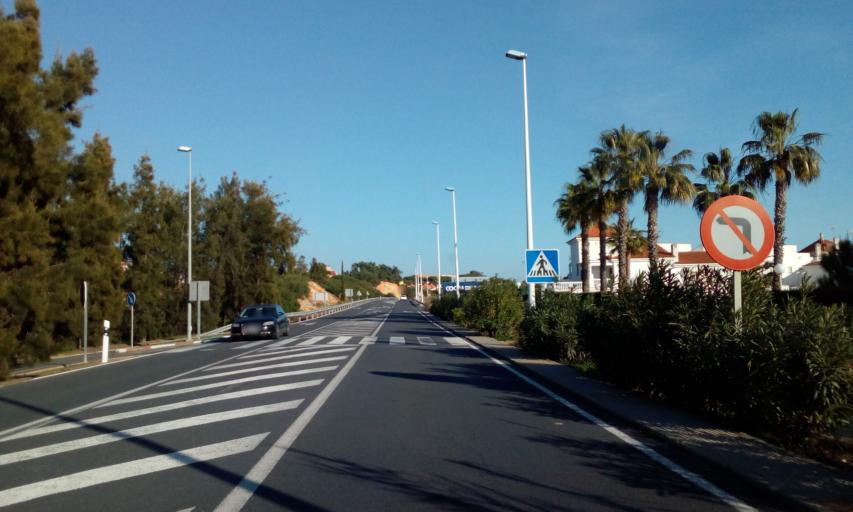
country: ES
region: Andalusia
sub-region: Provincia de Huelva
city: Lepe
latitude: 37.2088
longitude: -7.2487
